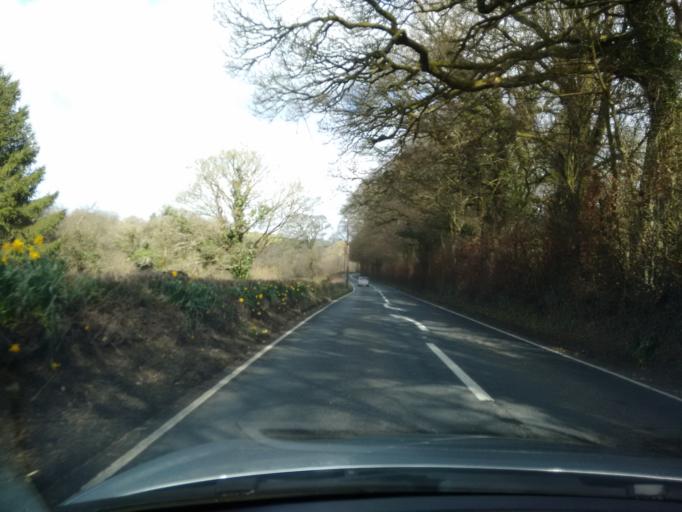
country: GB
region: England
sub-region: Cornwall
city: Launceston
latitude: 50.5983
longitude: -4.3368
